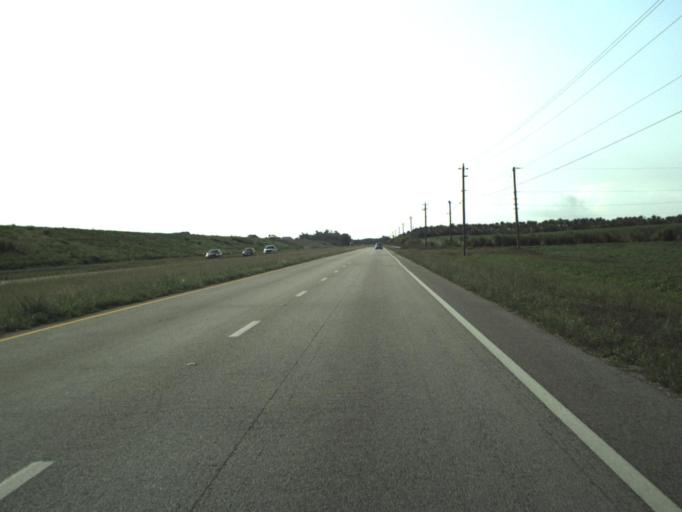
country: US
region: Florida
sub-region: Hendry County
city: Clewiston
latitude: 26.7071
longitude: -80.8315
